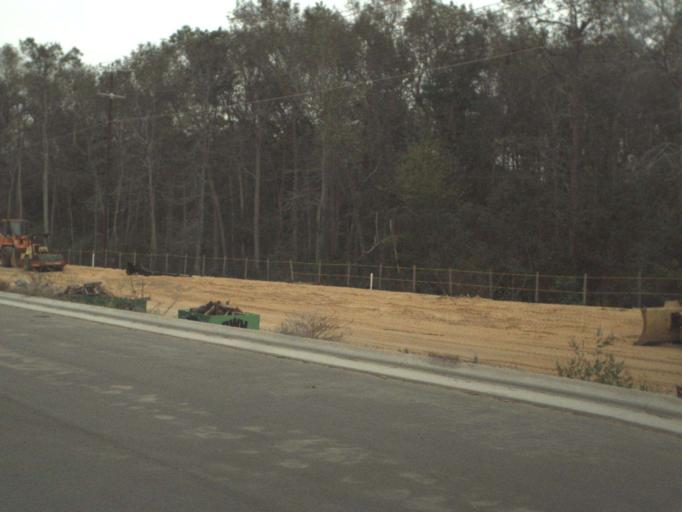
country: US
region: Florida
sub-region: Leon County
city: Tallahassee
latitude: 30.4461
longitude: -84.3550
